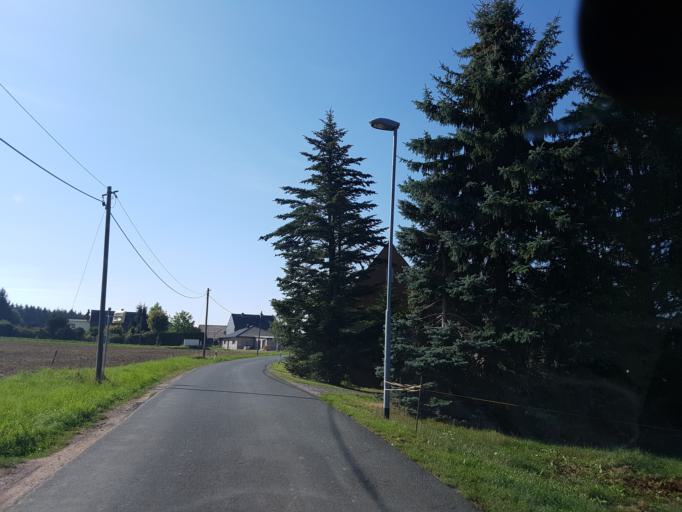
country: DE
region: Saxony
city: Kriebstein
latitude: 51.0587
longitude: 13.0094
